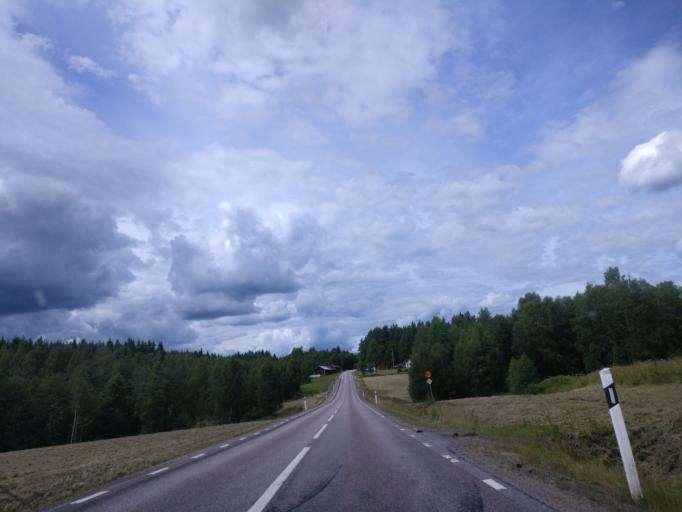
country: SE
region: Vaermland
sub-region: Hagfors Kommun
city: Ekshaerad
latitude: 60.1767
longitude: 13.3902
